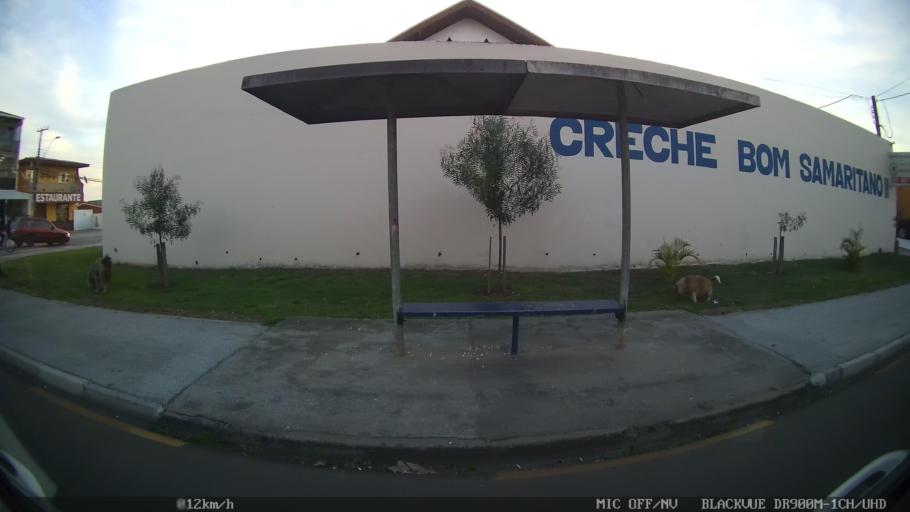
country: BR
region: Parana
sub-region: Pinhais
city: Pinhais
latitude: -25.4654
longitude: -49.1877
